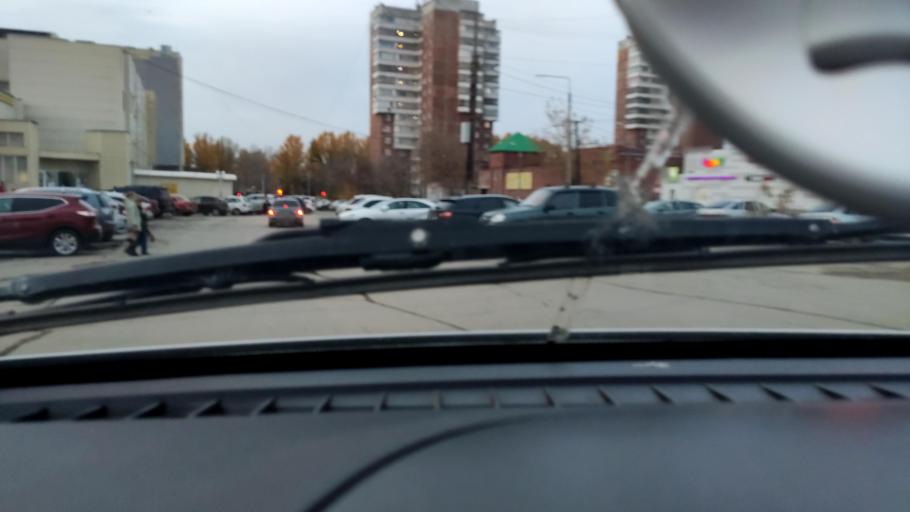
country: RU
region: Perm
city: Perm
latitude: 57.9771
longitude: 56.1906
